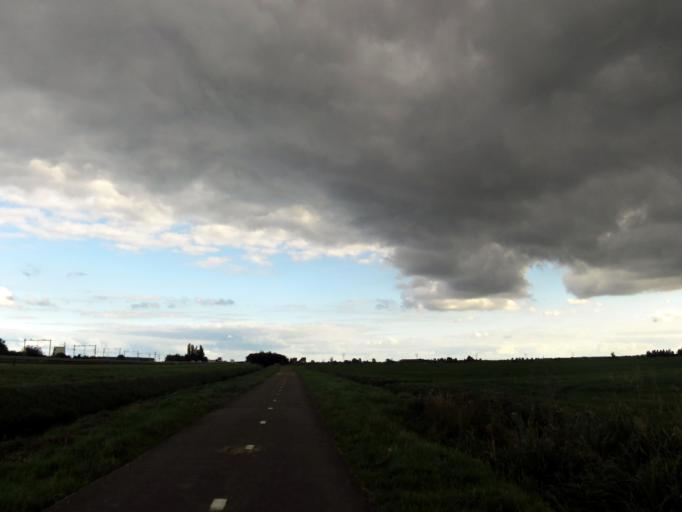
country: NL
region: South Holland
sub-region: Gemeente Leiderdorp
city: Leiderdorp
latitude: 52.1283
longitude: 4.5444
